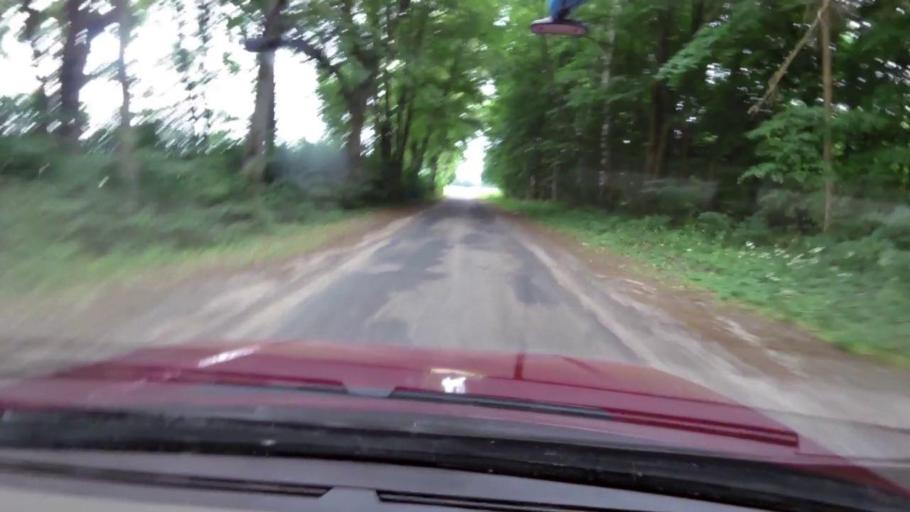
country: PL
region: Pomeranian Voivodeship
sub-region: Powiat slupski
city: Kepice
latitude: 54.1846
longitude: 16.7939
